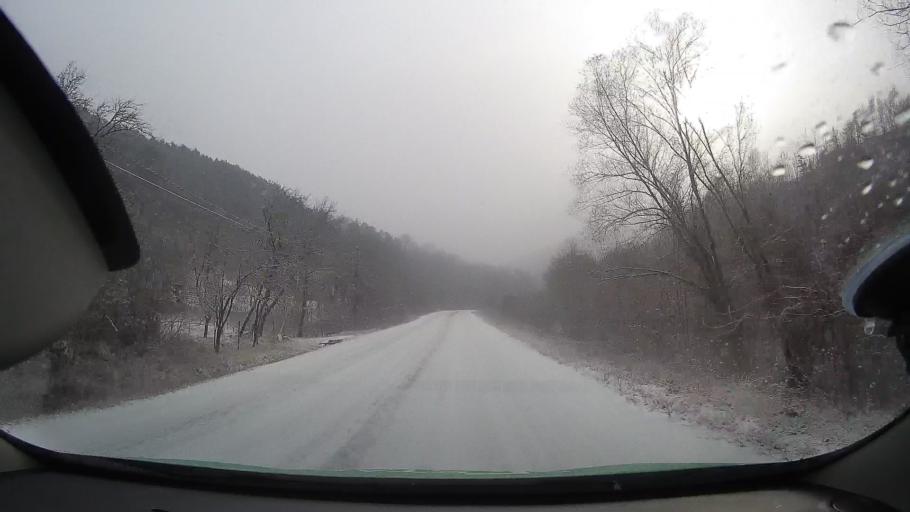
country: RO
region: Alba
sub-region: Comuna Livezile
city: Livezile
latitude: 46.3550
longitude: 23.6171
